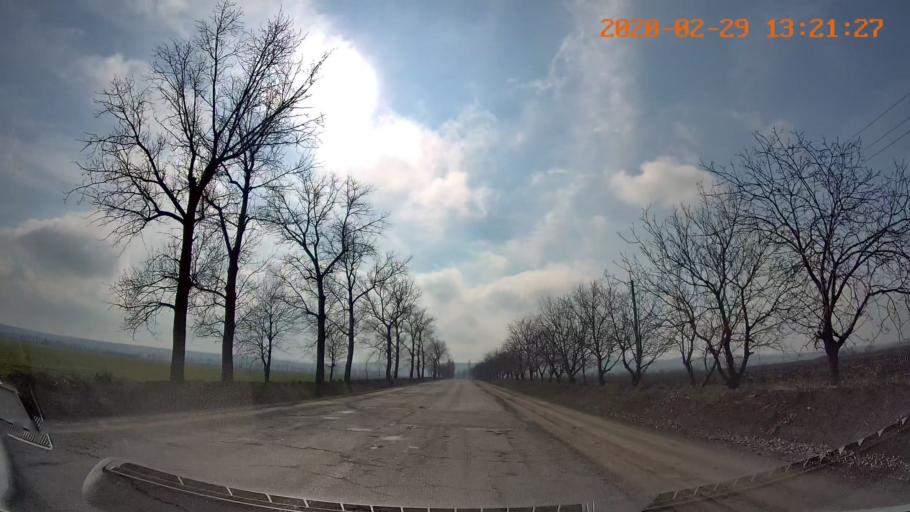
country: MD
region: Telenesti
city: Camenca
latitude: 47.9701
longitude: 28.6329
